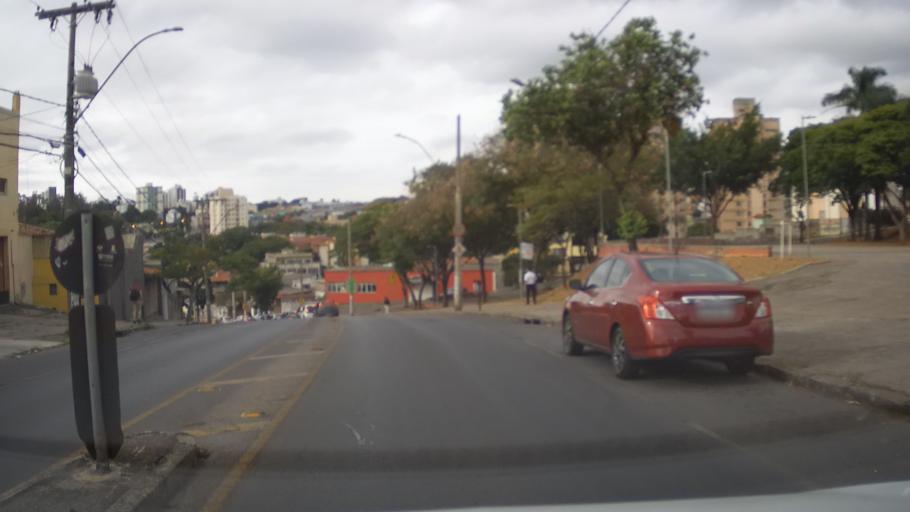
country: BR
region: Minas Gerais
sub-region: Belo Horizonte
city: Belo Horizonte
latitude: -19.8267
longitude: -43.9629
